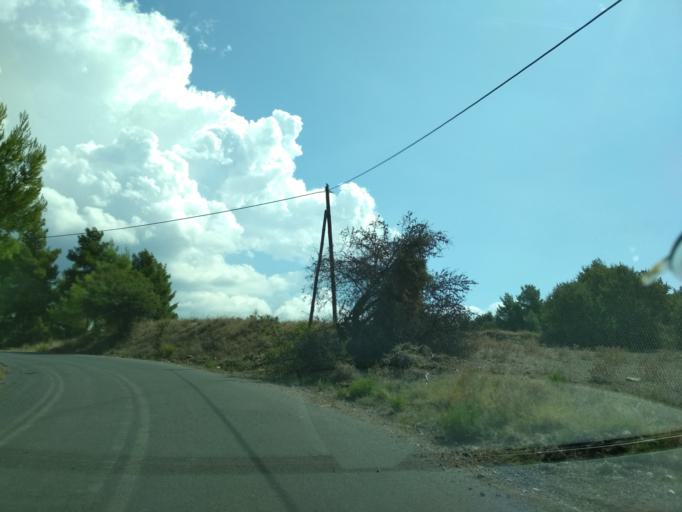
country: GR
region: Central Greece
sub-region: Nomos Evvoias
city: Roviai
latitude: 38.8155
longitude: 23.2755
